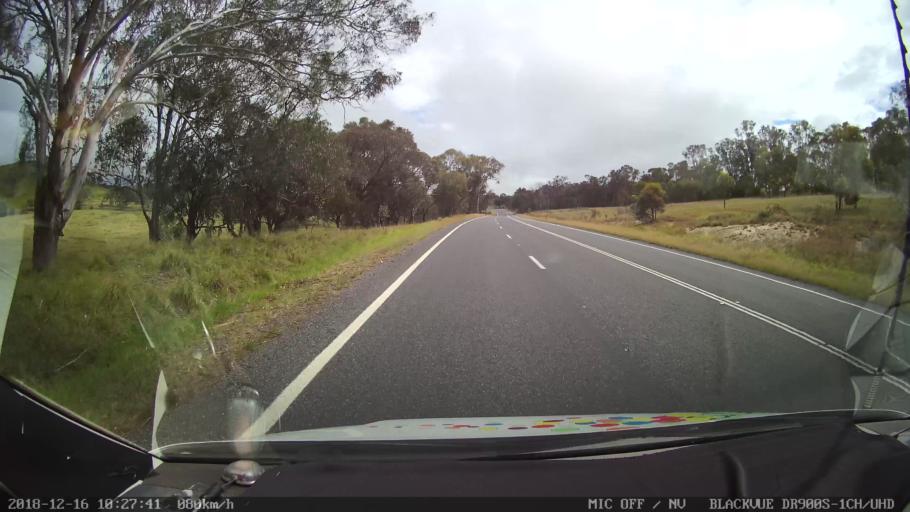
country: AU
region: New South Wales
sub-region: Tenterfield Municipality
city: Carrolls Creek
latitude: -29.1304
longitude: 151.9959
